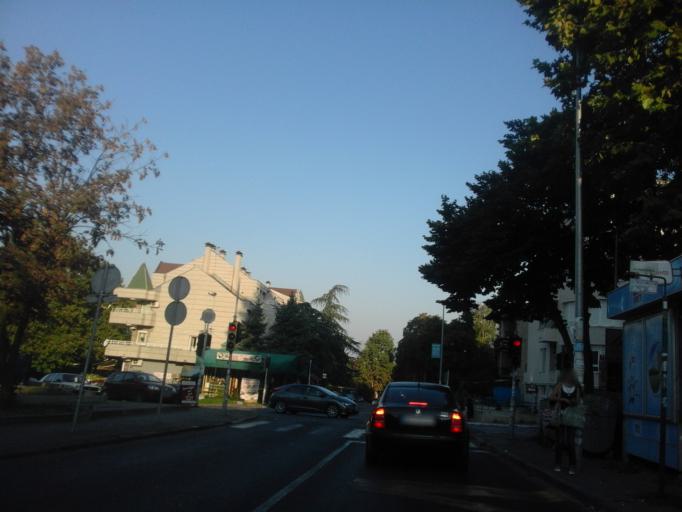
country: RS
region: Central Serbia
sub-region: Belgrade
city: Cukarica
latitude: 44.7679
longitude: 20.4206
